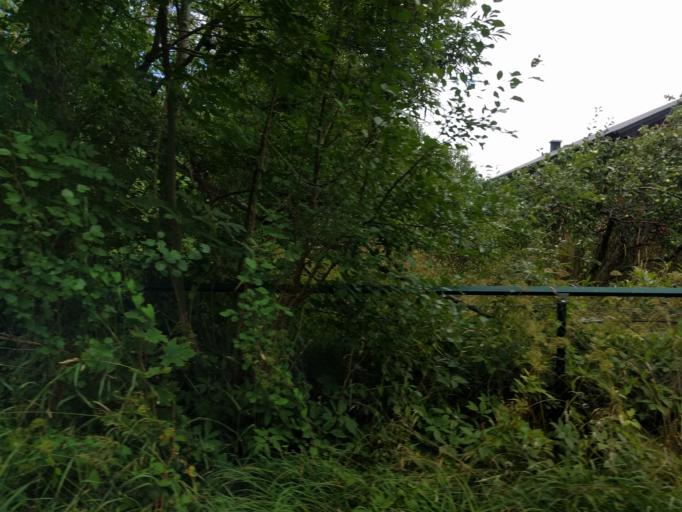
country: SE
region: Soedermanland
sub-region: Oxelosunds Kommun
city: Bara
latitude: 58.4907
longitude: 16.9346
